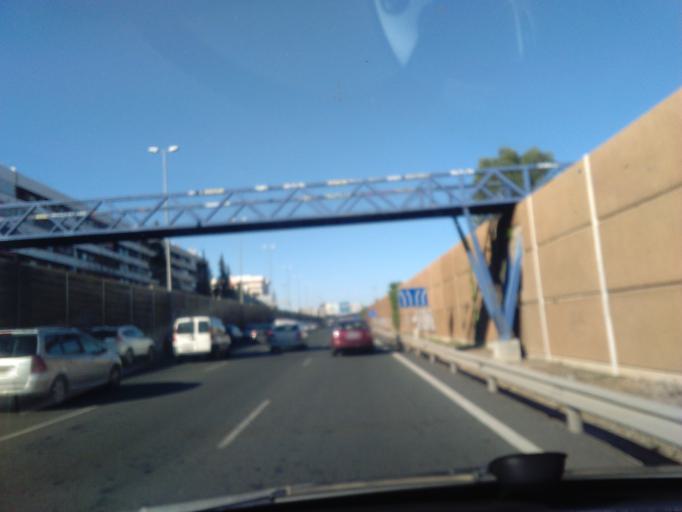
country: ES
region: Andalusia
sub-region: Provincia de Sevilla
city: Sevilla
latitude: 37.4031
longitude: -5.9472
